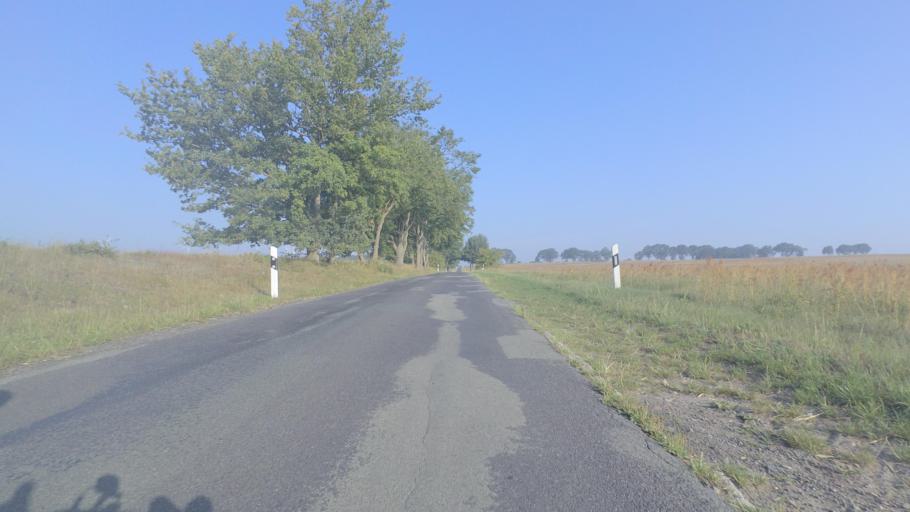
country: DE
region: Brandenburg
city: Heiligengrabe
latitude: 53.2542
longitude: 12.3420
